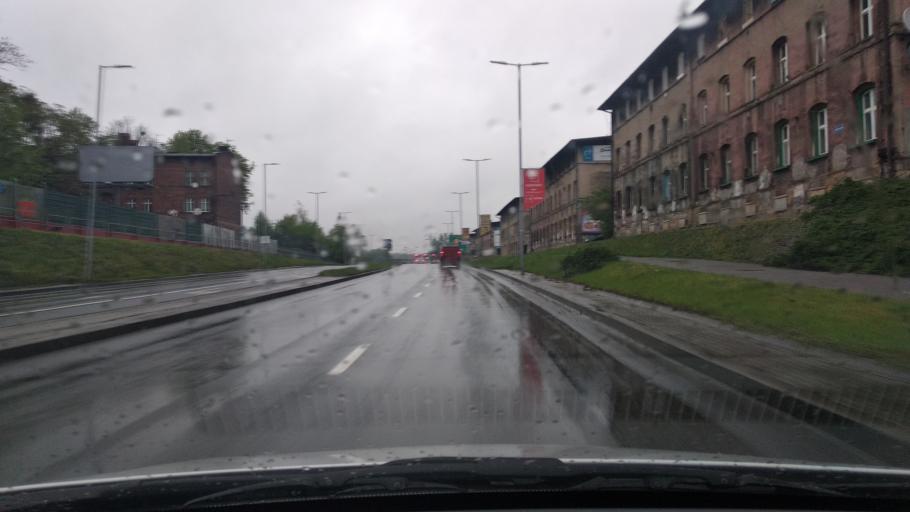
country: PL
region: Silesian Voivodeship
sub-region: Katowice
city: Katowice
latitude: 50.2651
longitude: 18.9884
